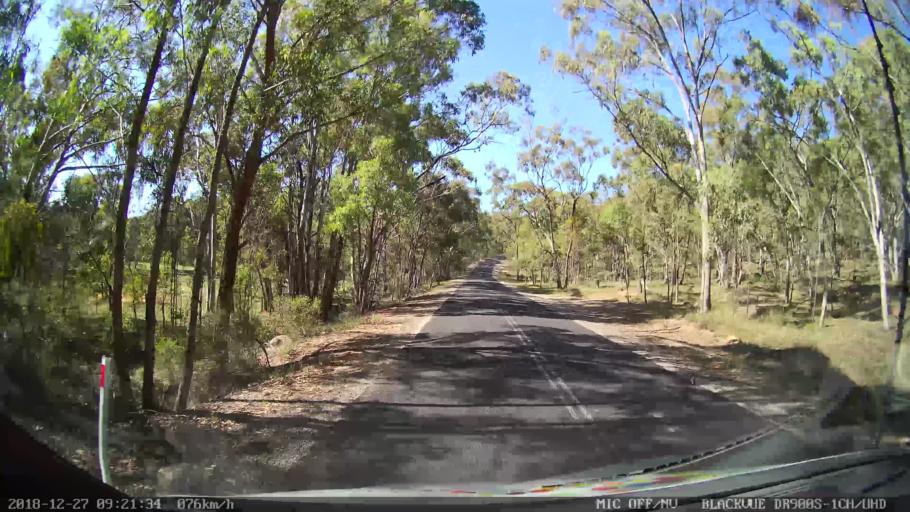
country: AU
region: New South Wales
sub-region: Lithgow
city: Portland
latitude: -33.1250
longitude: 150.0159
